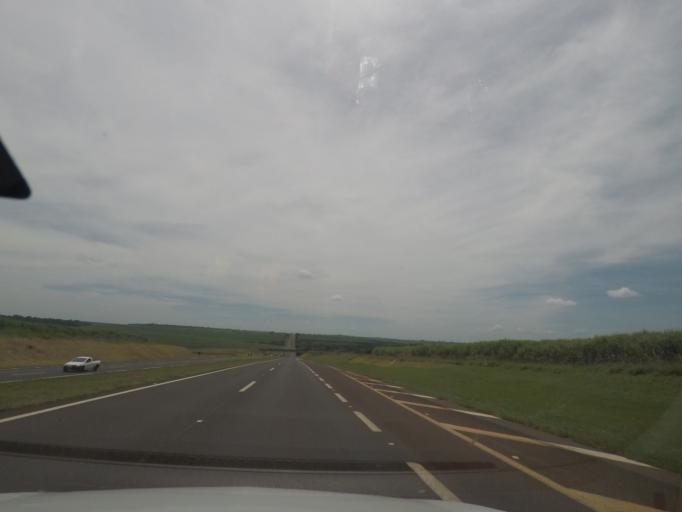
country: BR
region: Sao Paulo
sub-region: Bebedouro
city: Bebedouro
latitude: -21.0424
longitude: -48.4170
